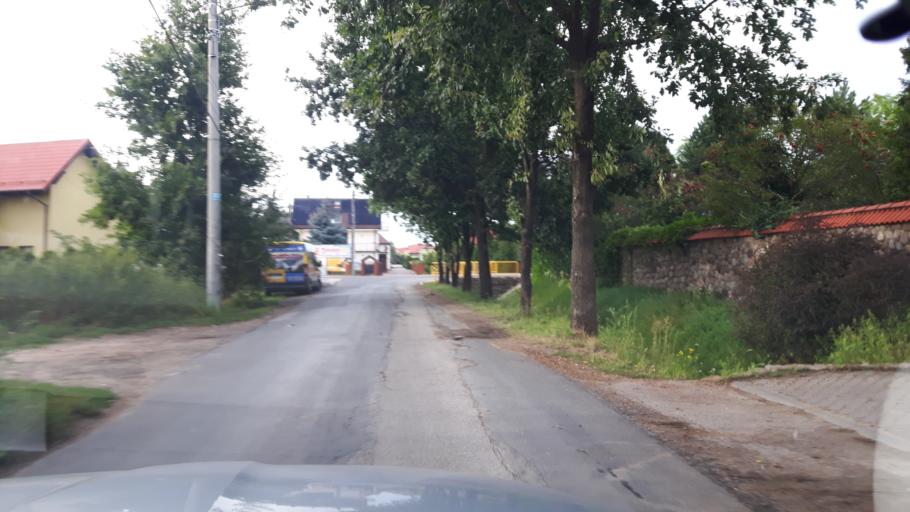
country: PL
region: Masovian Voivodeship
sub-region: Powiat wolominski
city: Marki
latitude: 52.3205
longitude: 21.0901
